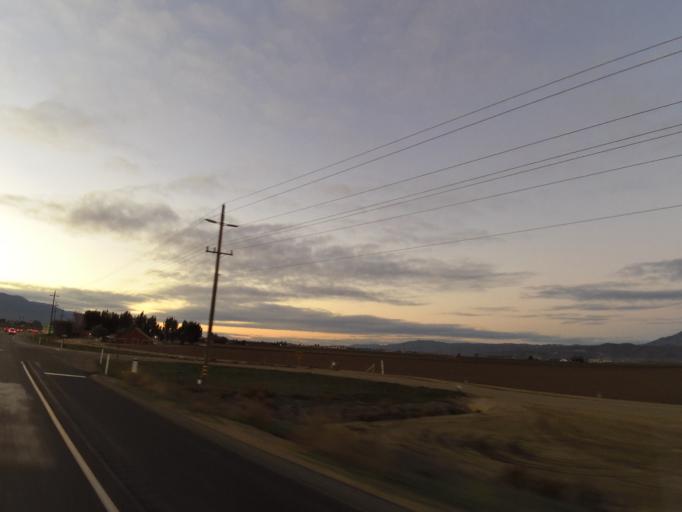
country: US
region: California
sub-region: Monterey County
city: Greenfield
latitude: 36.2980
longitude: -121.2131
